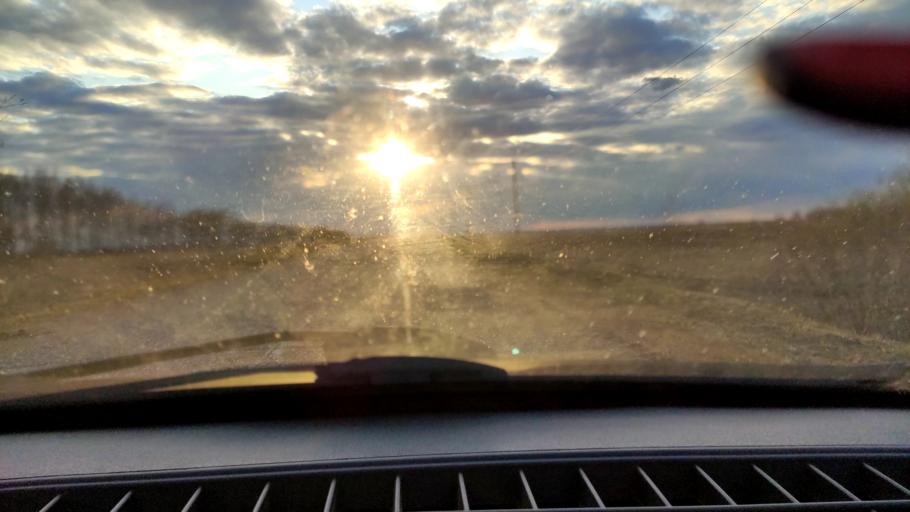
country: RU
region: Bashkortostan
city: Tolbazy
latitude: 54.0089
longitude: 55.5972
